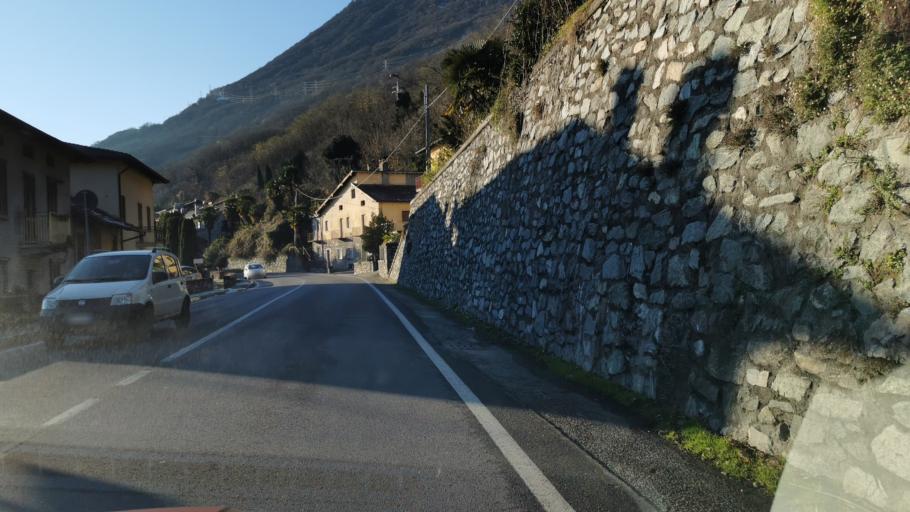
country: IT
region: Lombardy
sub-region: Provincia di Como
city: Aurogna
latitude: 46.1693
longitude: 9.3601
